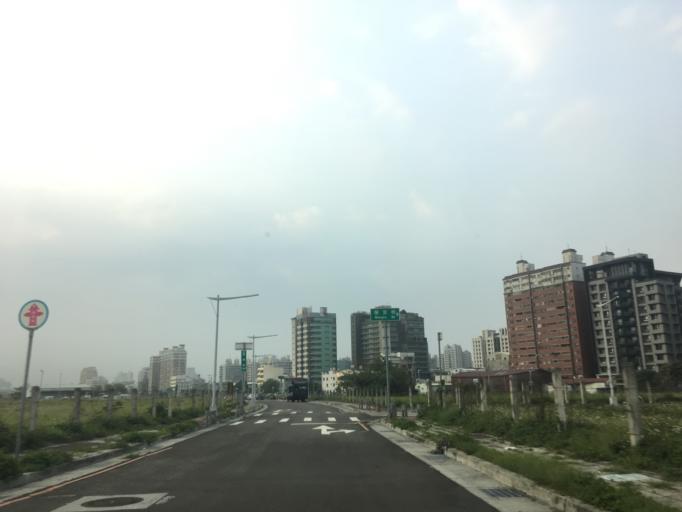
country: TW
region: Taiwan
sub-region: Taichung City
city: Taichung
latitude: 24.1946
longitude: 120.6674
